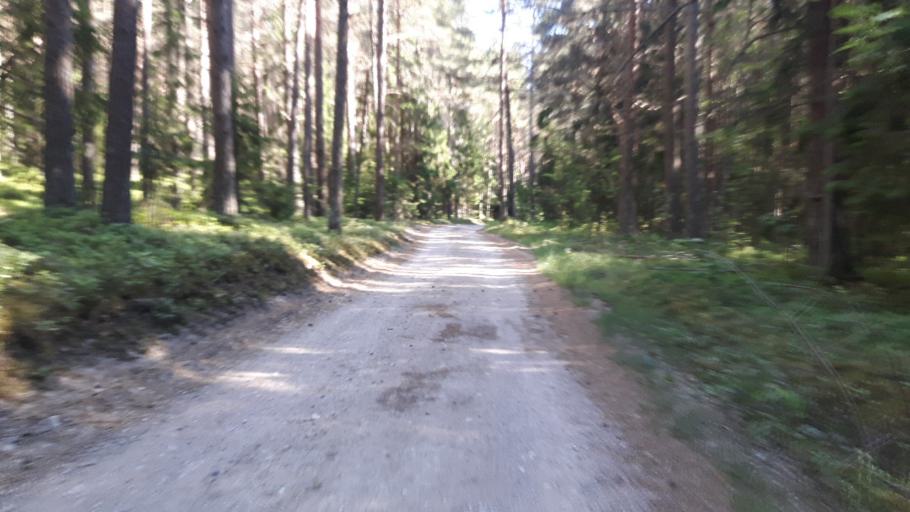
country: LV
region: Salacgrivas
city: Salacgriva
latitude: 57.7288
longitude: 24.3497
